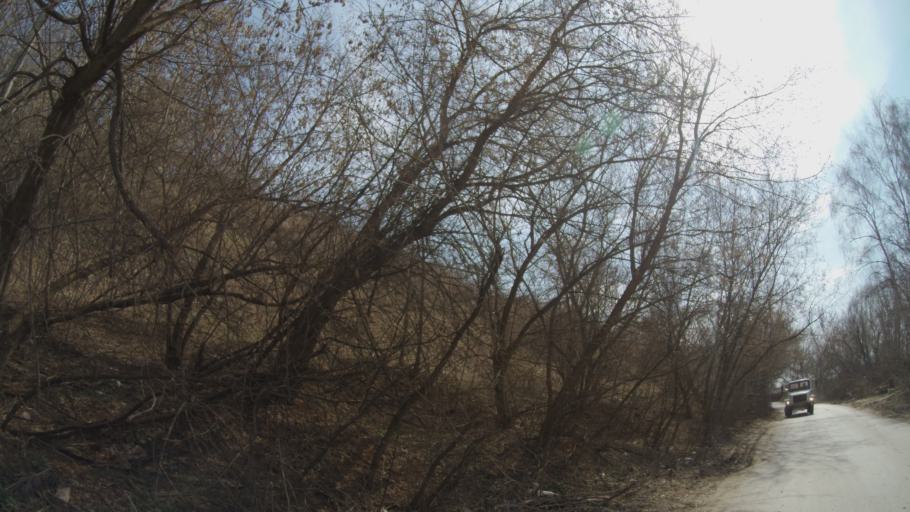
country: RU
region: Nizjnij Novgorod
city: Vyyezdnoye
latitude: 55.3872
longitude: 43.8104
